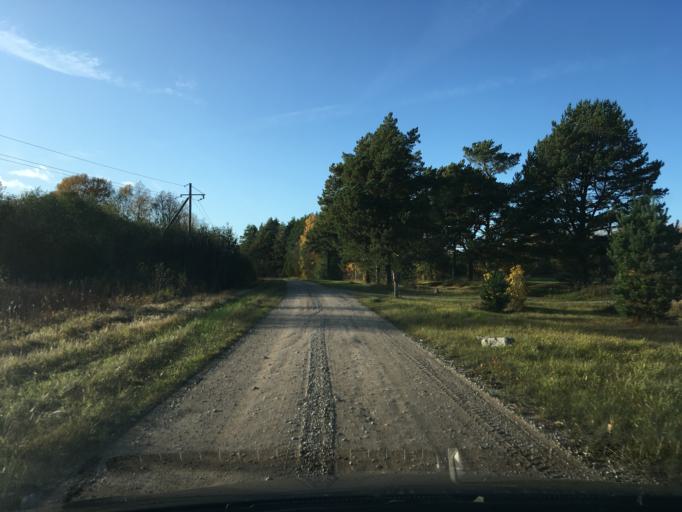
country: EE
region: Laeaene
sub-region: Lihula vald
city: Lihula
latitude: 58.5675
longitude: 23.7627
